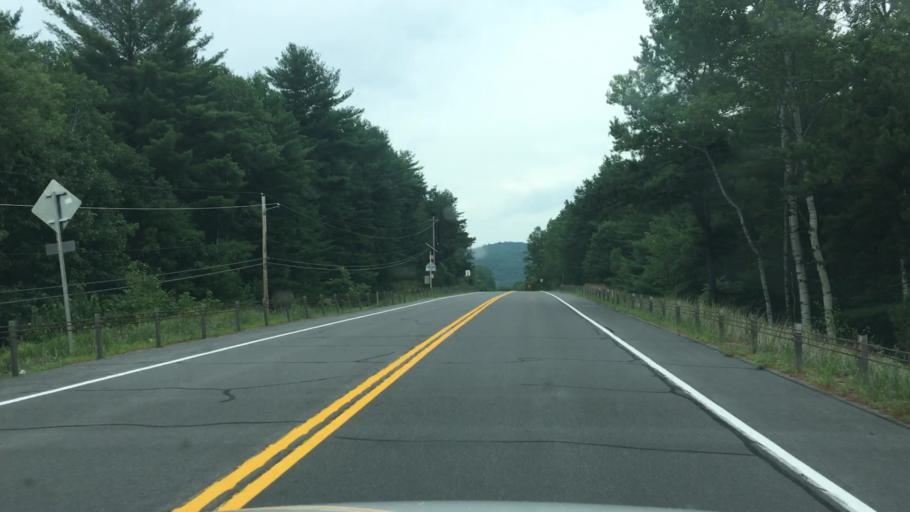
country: US
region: New York
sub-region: Essex County
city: Keeseville
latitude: 44.4651
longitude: -73.5932
